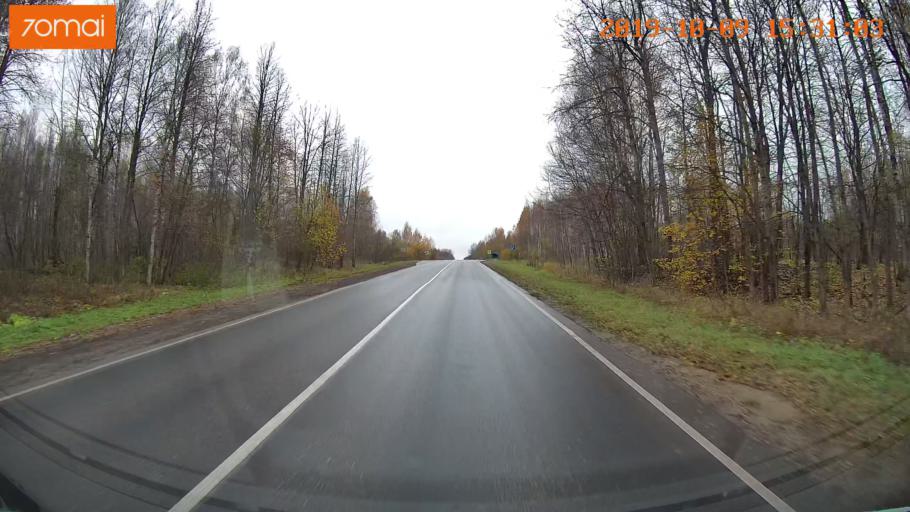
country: RU
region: Kostroma
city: Susanino
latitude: 57.9742
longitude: 41.3121
